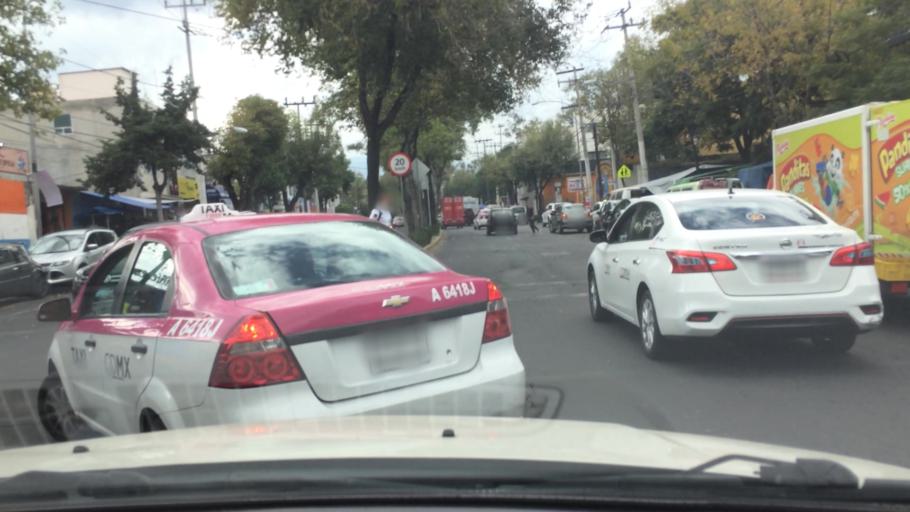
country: MX
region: Mexico City
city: Tlalpan
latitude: 19.2953
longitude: -99.1794
